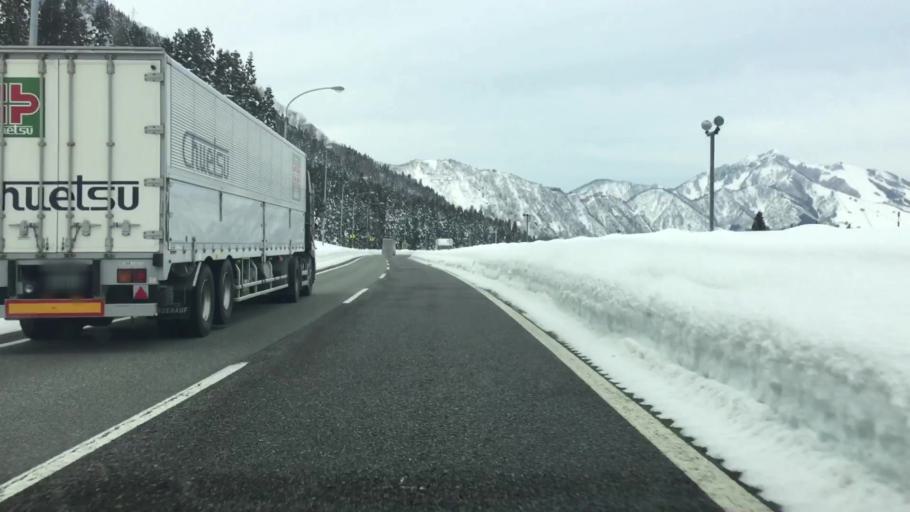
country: JP
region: Niigata
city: Shiozawa
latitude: 36.8912
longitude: 138.8473
